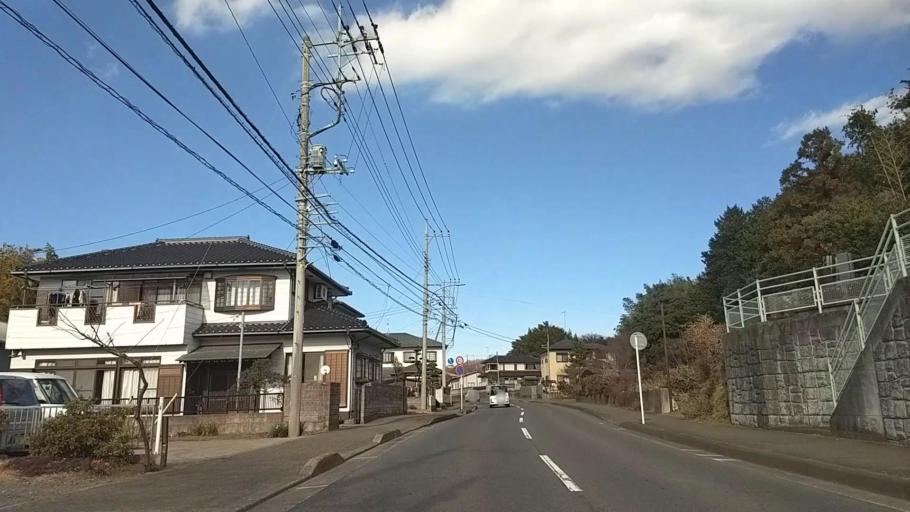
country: JP
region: Kanagawa
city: Isehara
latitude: 35.4206
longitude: 139.3023
